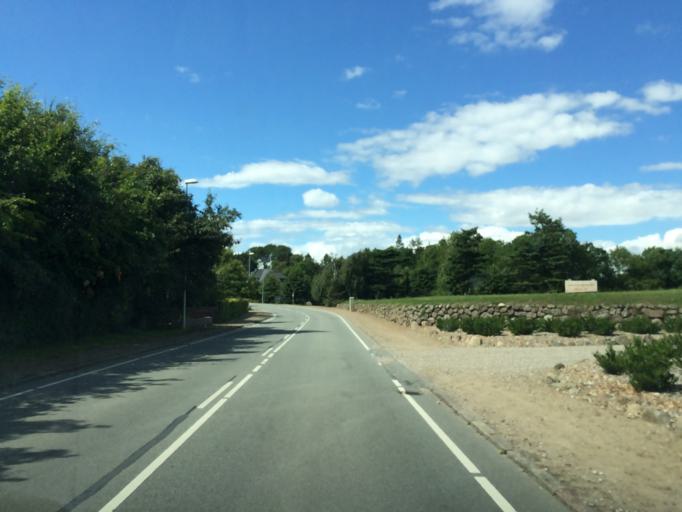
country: DK
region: South Denmark
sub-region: Faaborg-Midtfyn Kommune
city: Faaborg
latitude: 55.1360
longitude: 10.1973
